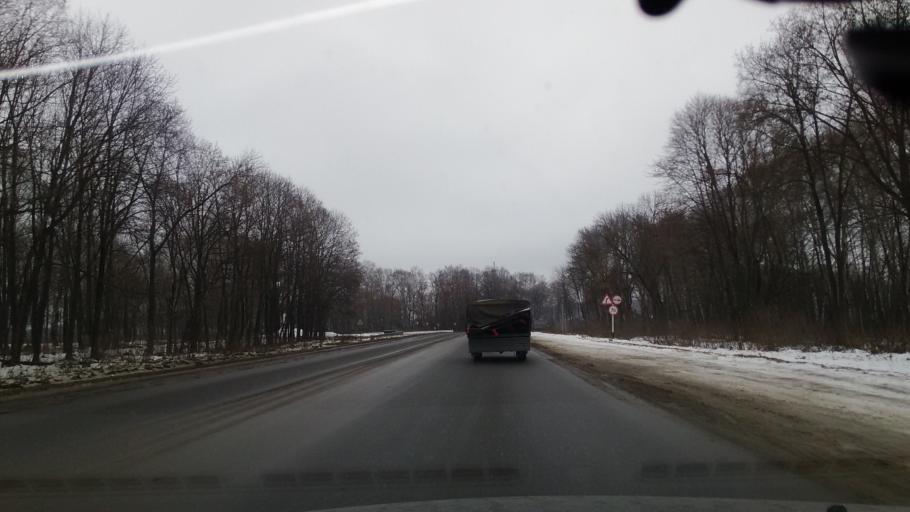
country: RU
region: Tula
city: Tula
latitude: 54.1397
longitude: 37.6711
